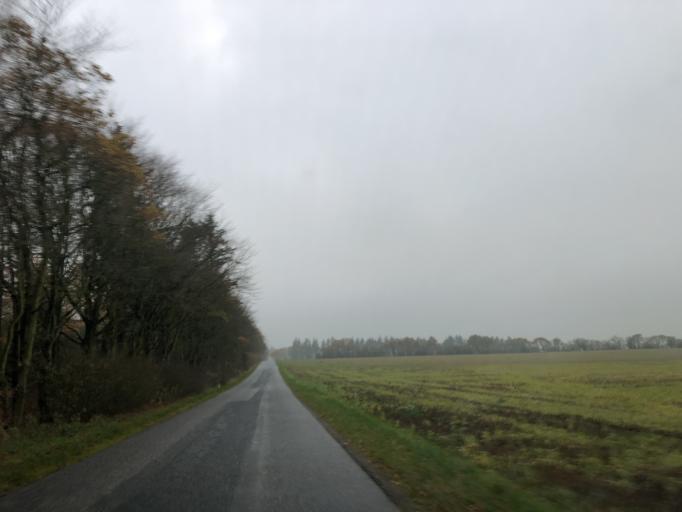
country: DK
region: Central Jutland
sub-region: Herning Kommune
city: Vildbjerg
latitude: 56.2004
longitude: 8.6692
